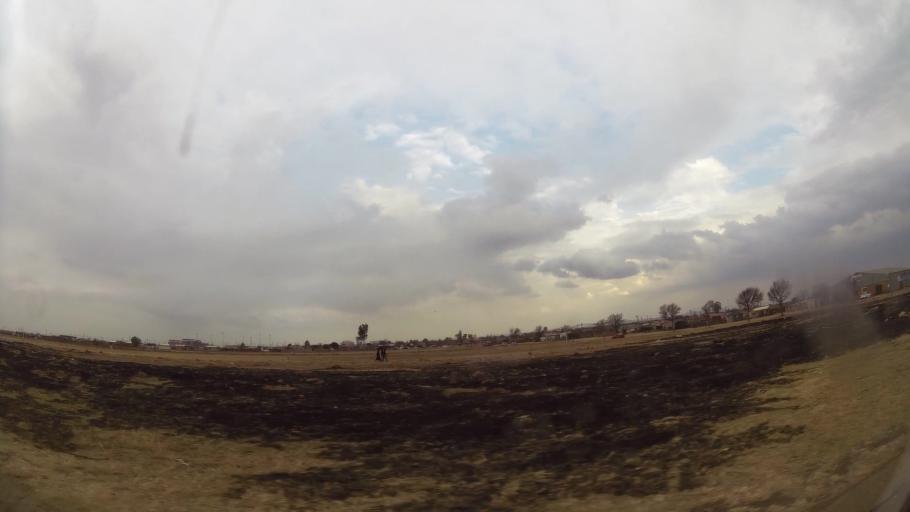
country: ZA
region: Gauteng
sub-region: Ekurhuleni Metropolitan Municipality
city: Germiston
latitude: -26.3844
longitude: 28.1333
